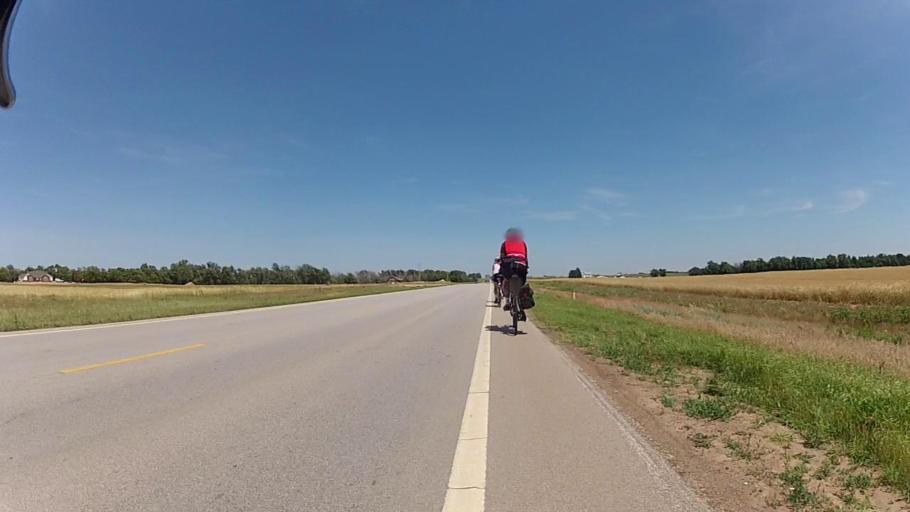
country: US
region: Kansas
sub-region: Harper County
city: Harper
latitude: 37.2386
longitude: -98.1257
